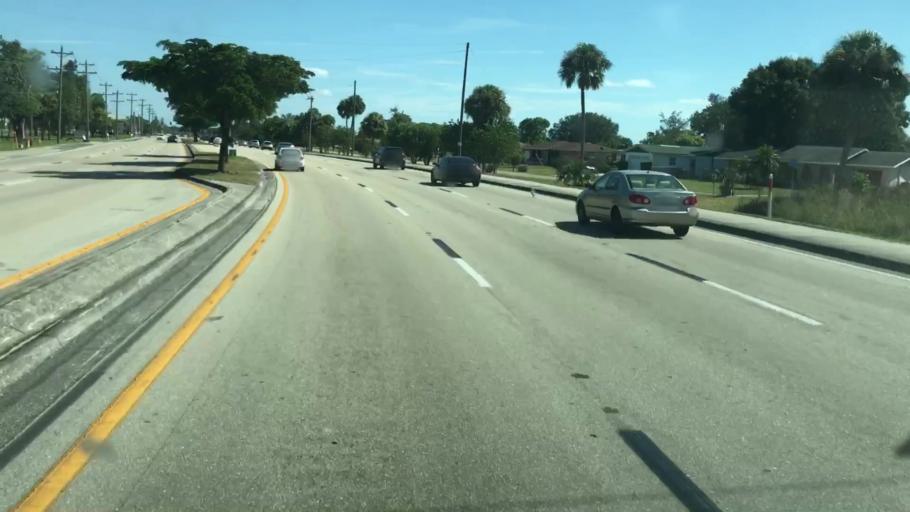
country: US
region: Florida
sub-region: Lee County
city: Lehigh Acres
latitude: 26.6142
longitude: -81.6624
